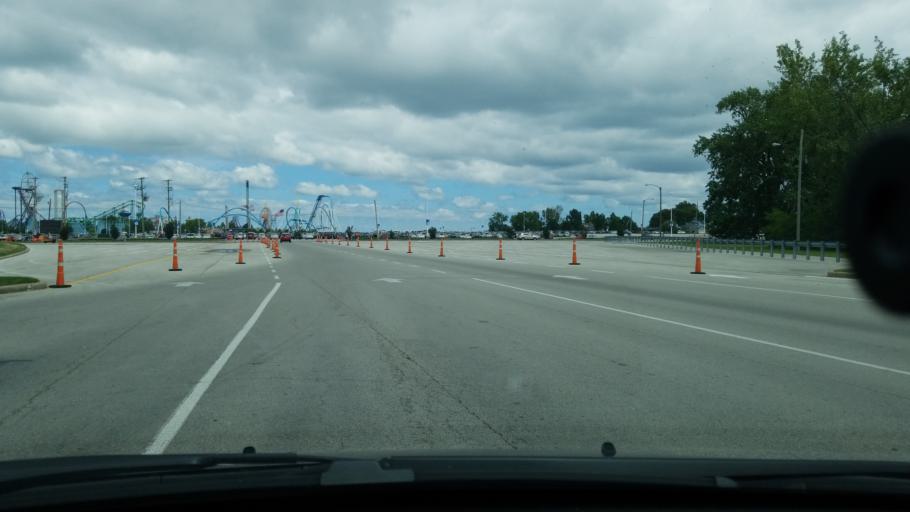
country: US
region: Ohio
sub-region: Erie County
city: Sandusky
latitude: 41.4718
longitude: -82.6765
